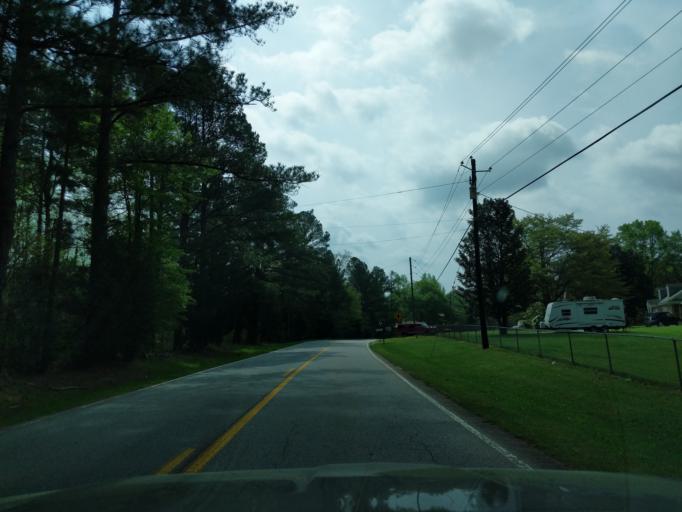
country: US
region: Georgia
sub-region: Columbia County
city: Appling
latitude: 33.5588
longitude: -82.3190
